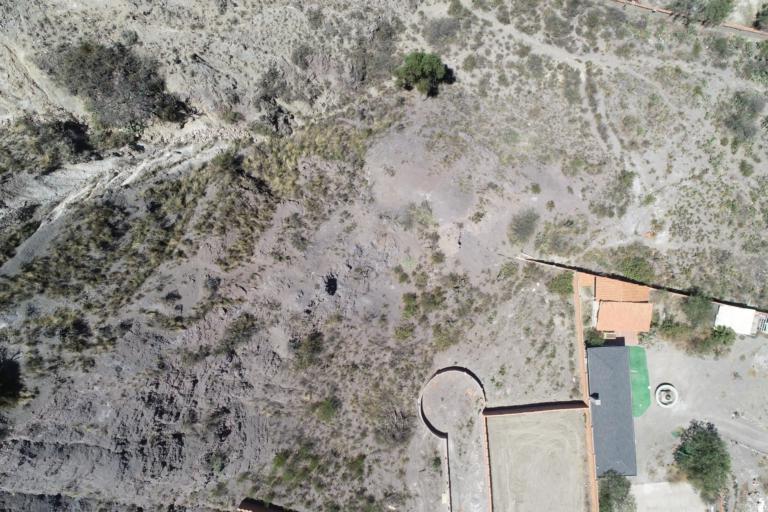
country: BO
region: La Paz
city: La Paz
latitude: -16.6191
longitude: -68.0564
